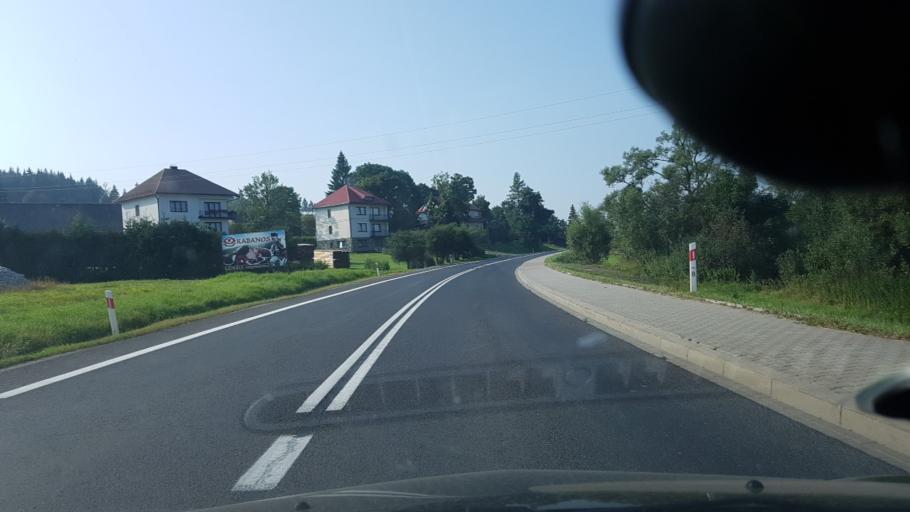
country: PL
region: Lesser Poland Voivodeship
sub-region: Powiat nowotarski
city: Podwilk
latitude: 49.5352
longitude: 19.7158
